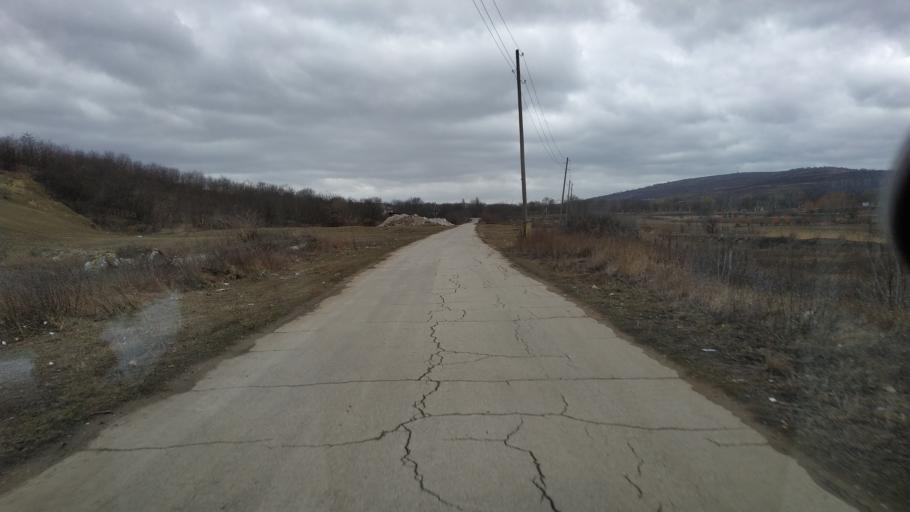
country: MD
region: Calarasi
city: Calarasi
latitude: 47.2446
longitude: 28.2920
